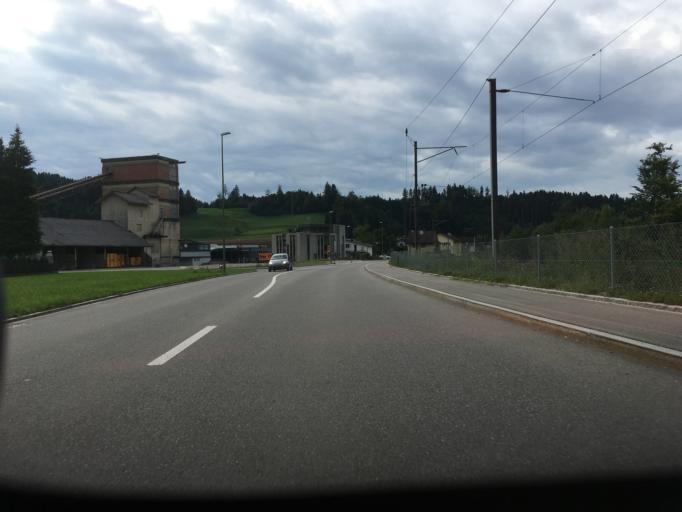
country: CH
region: Zurich
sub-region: Bezirk Pfaeffikon
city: Bauma
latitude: 47.3793
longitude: 8.8619
